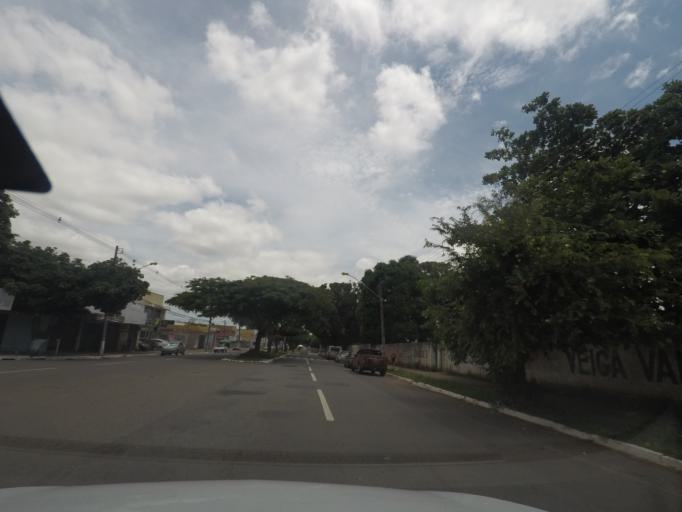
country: BR
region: Goias
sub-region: Goiania
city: Goiania
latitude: -16.6689
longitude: -49.2441
